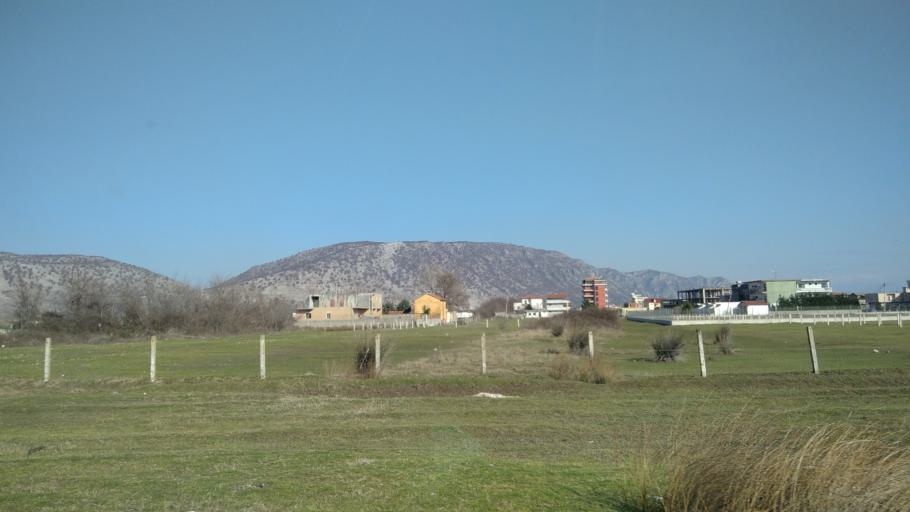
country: AL
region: Shkoder
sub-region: Rrethi i Shkodres
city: Velipoje
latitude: 41.8693
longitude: 19.4212
